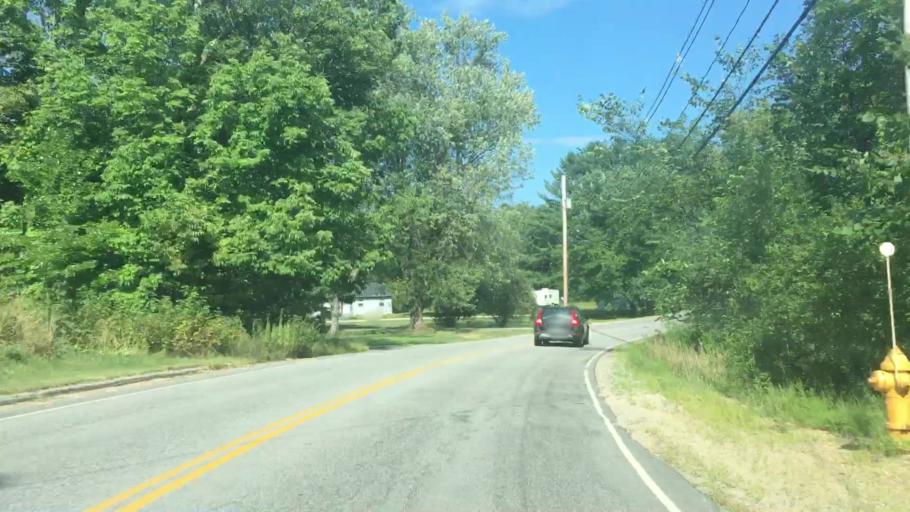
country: US
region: Maine
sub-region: Oxford County
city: Oxford
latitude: 44.1363
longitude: -70.4931
